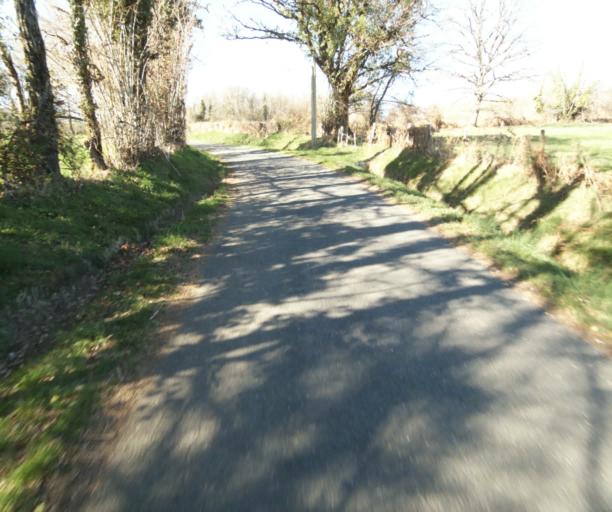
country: FR
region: Limousin
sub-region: Departement de la Correze
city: Chamboulive
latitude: 45.4065
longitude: 1.6505
